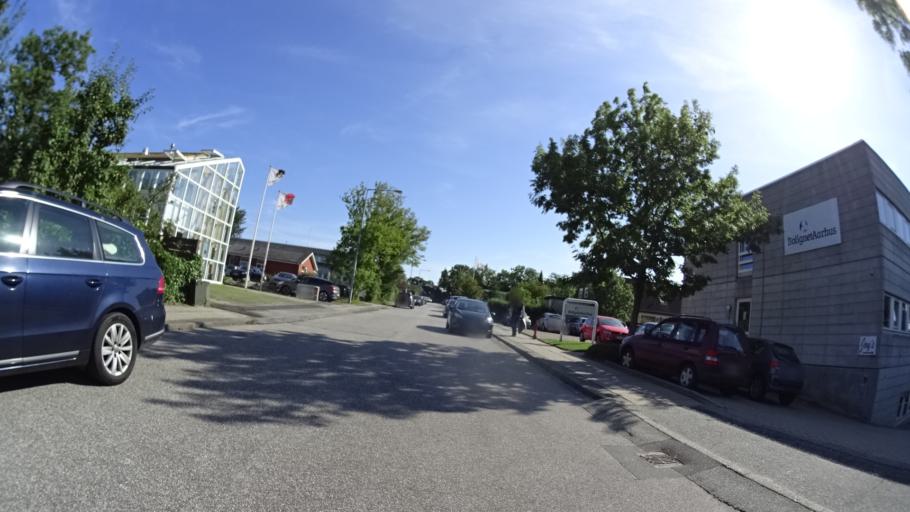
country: DK
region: Central Jutland
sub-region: Arhus Kommune
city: Stavtrup
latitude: 56.1423
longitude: 10.1505
